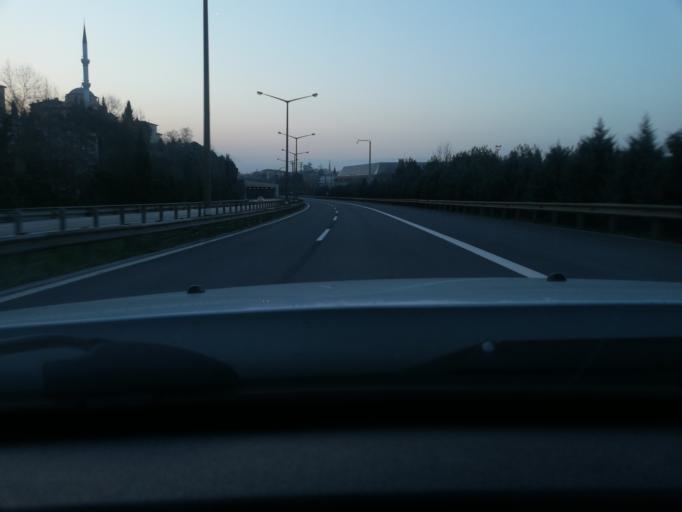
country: TR
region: Kocaeli
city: Derince
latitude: 40.7643
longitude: 29.8554
